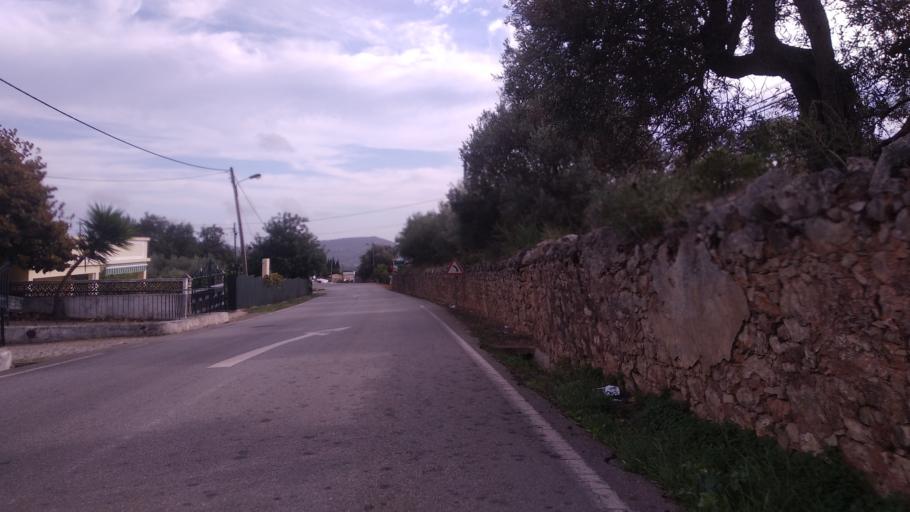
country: PT
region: Faro
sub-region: Sao Bras de Alportel
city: Sao Bras de Alportel
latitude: 37.1604
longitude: -7.8996
